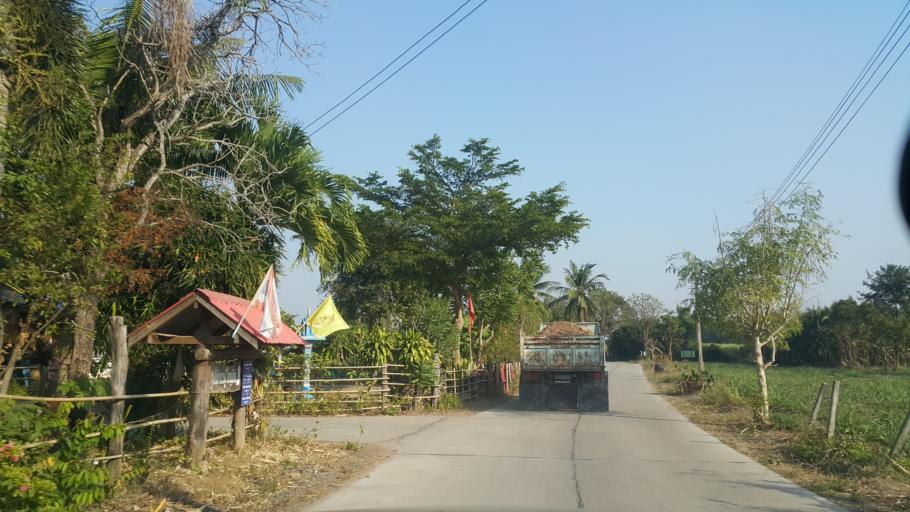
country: TH
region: Nakhon Ratchasima
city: Chakkarat
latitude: 15.0679
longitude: 102.3987
